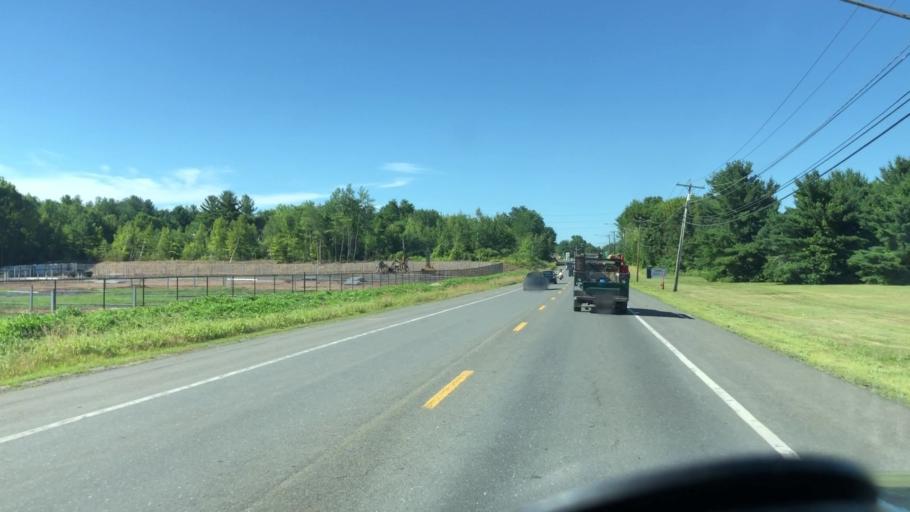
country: US
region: Massachusetts
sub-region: Hampshire County
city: Southampton
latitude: 42.1773
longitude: -72.7270
